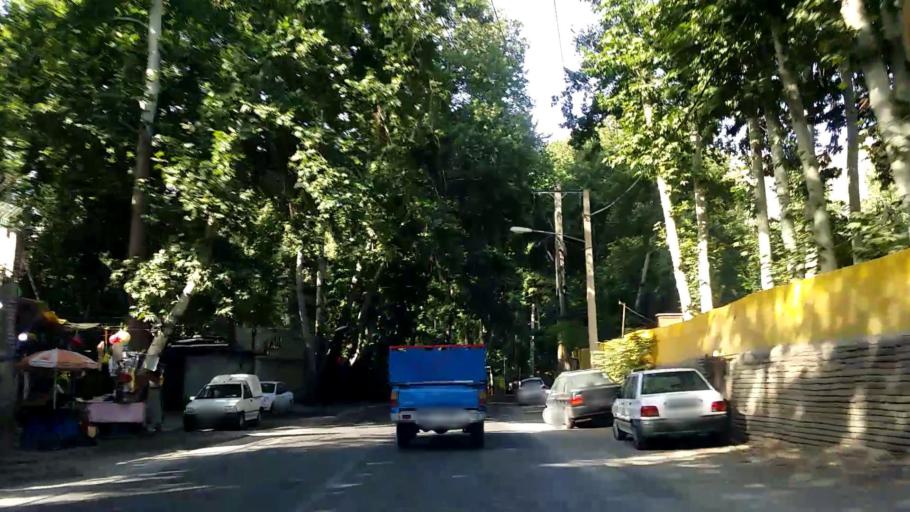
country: IR
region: Alborz
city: Karaj
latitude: 35.8910
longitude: 51.0452
